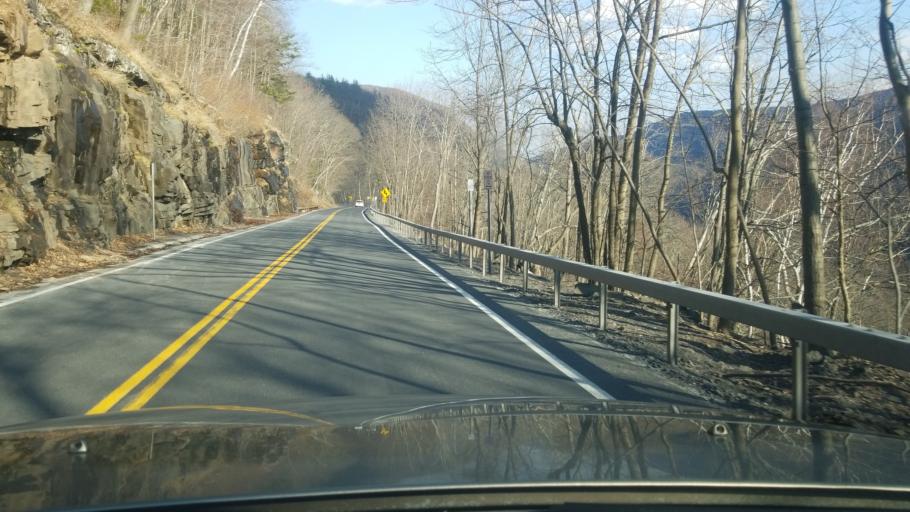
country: US
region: New York
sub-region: Greene County
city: Palenville
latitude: 42.1939
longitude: -74.0836
